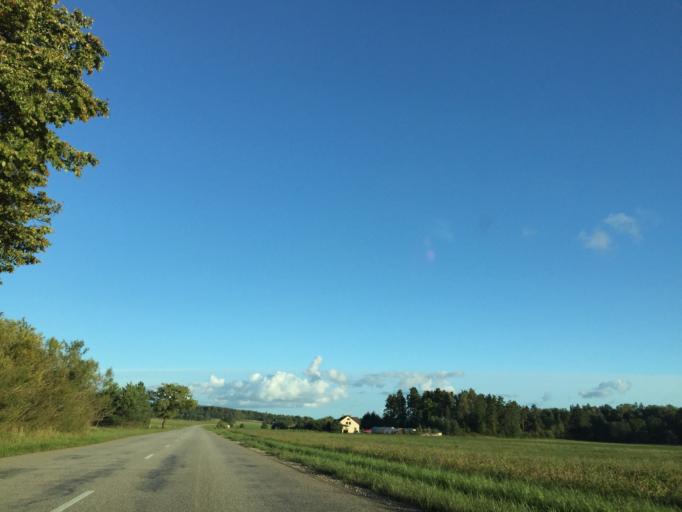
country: LV
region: Kuldigas Rajons
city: Kuldiga
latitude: 56.9321
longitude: 22.0391
